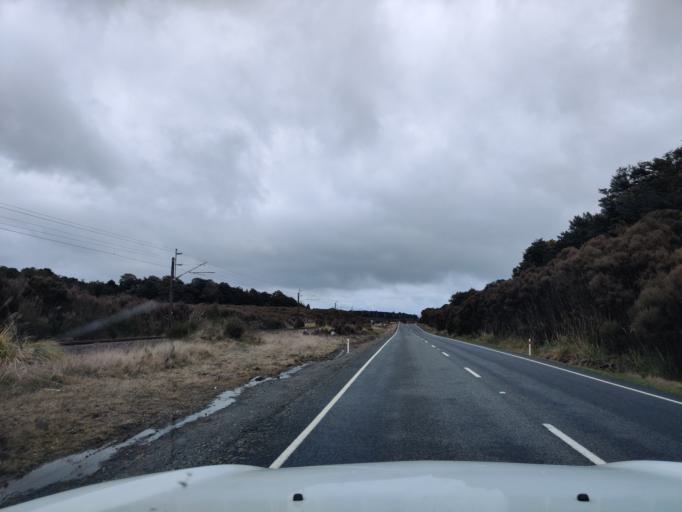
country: NZ
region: Manawatu-Wanganui
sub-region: Ruapehu District
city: Waiouru
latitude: -39.3197
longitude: 175.3863
